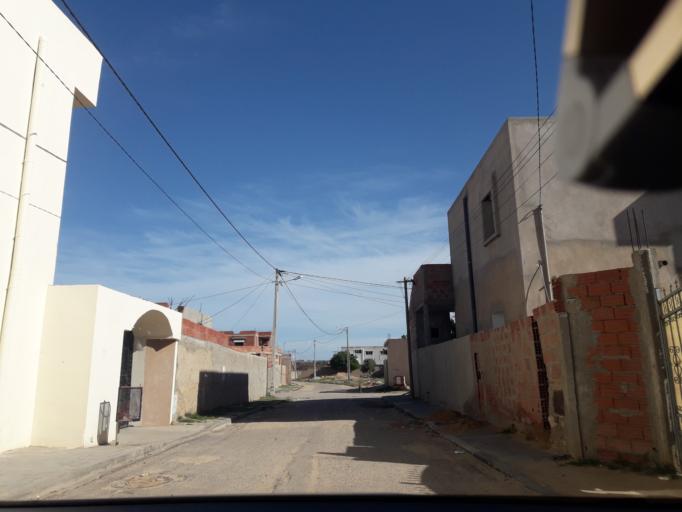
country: TN
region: Safaqis
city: Sfax
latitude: 34.7380
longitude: 10.5206
